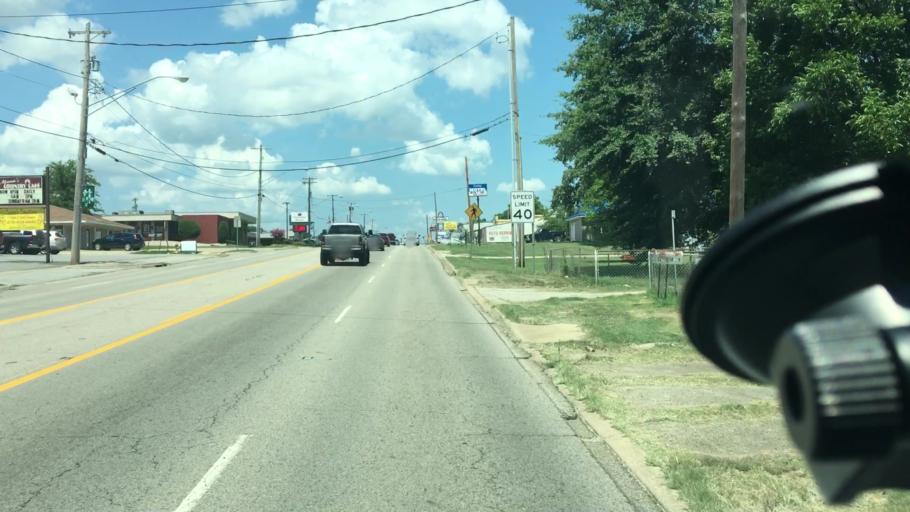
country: US
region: Arkansas
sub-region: Sebastian County
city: Barling
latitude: 35.3238
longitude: -94.2980
